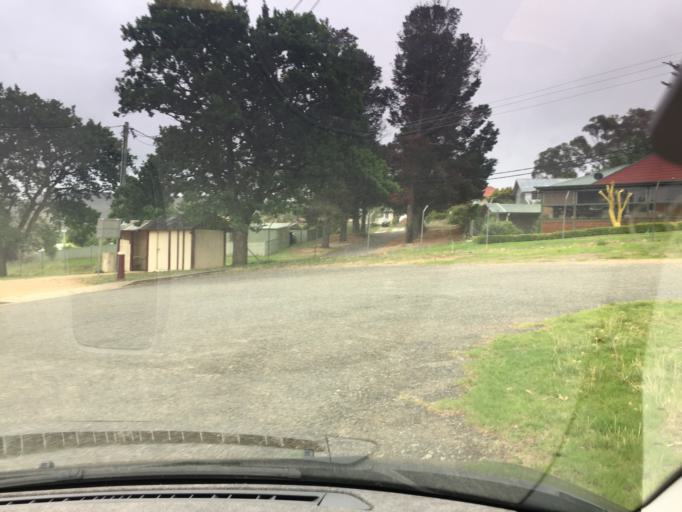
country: AU
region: New South Wales
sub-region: Cooma-Monaro
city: Cooma
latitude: -36.2391
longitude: 149.1221
